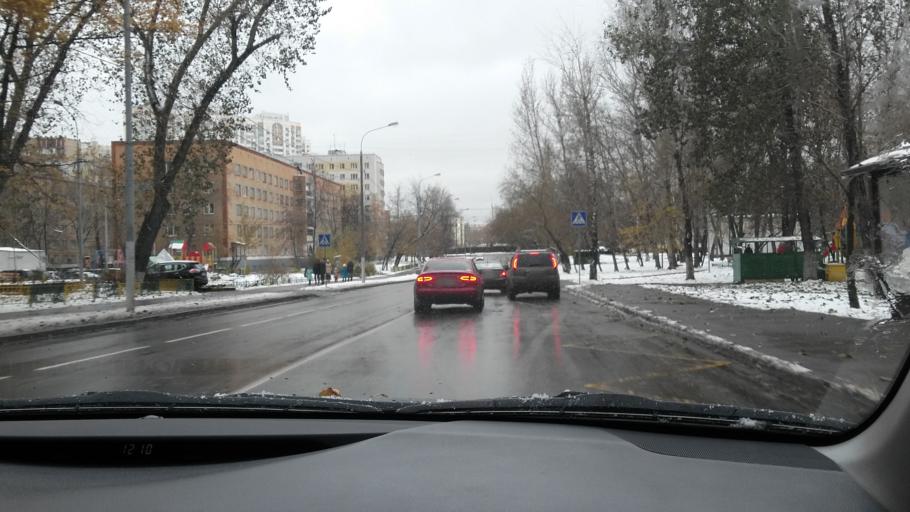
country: RU
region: Moscow
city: Novyye Kuz'minki
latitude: 55.7110
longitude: 37.7625
